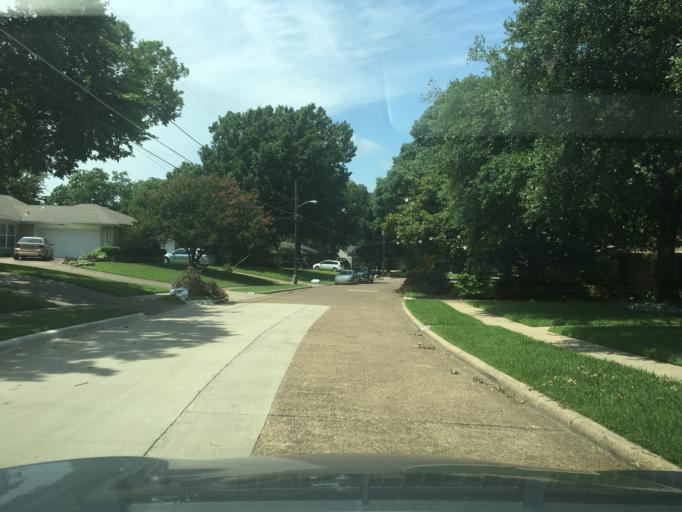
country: US
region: Texas
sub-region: Dallas County
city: Richardson
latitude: 32.9425
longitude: -96.7538
